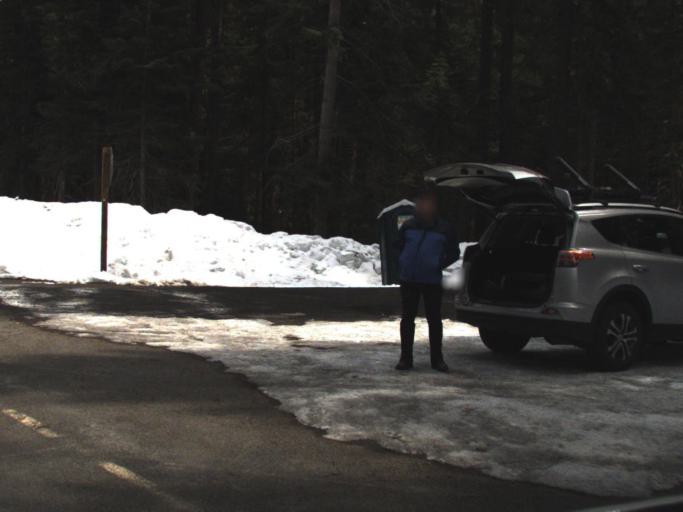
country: US
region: Washington
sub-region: Kittitas County
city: Cle Elum
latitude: 46.9445
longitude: -121.3281
